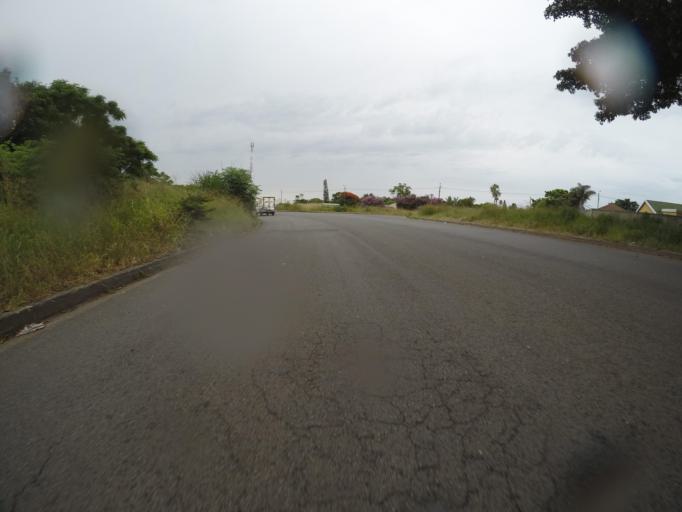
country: ZA
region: Eastern Cape
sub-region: Buffalo City Metropolitan Municipality
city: East London
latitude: -32.9674
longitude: 27.8295
